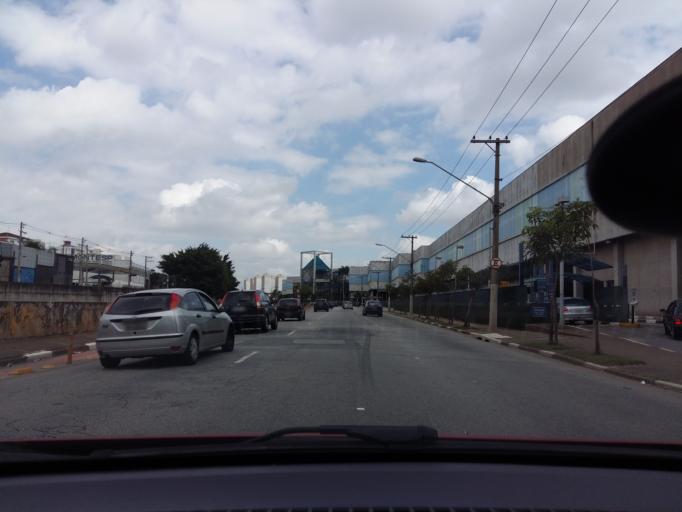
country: BR
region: Sao Paulo
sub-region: Sao Caetano Do Sul
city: Sao Caetano do Sul
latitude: -23.5913
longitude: -46.5873
